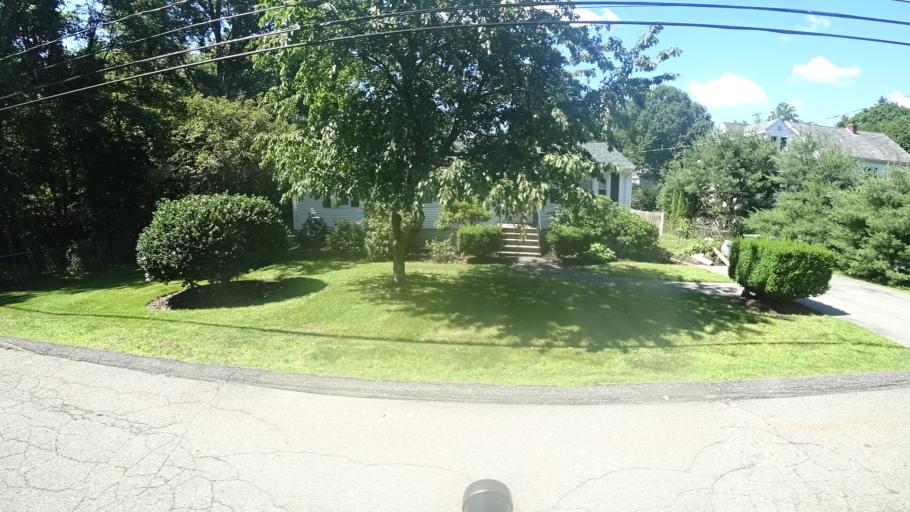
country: US
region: Massachusetts
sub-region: Norfolk County
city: Dedham
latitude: 42.2566
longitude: -71.1496
